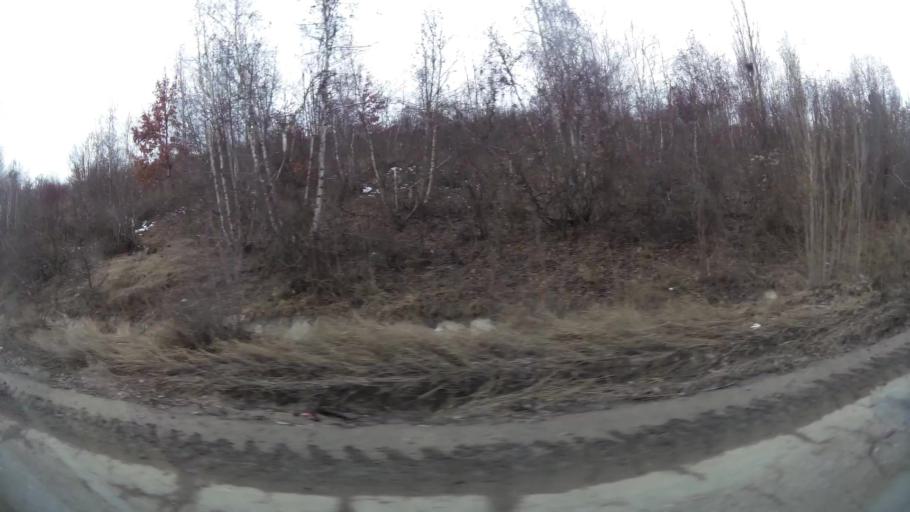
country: BG
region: Sofiya
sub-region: Obshtina Bozhurishte
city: Bozhurishte
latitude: 42.7104
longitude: 23.2303
